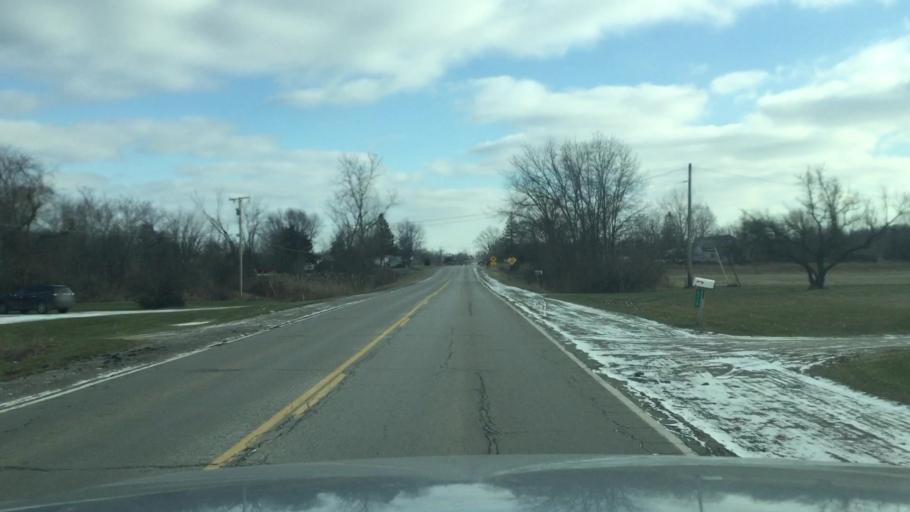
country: US
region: Michigan
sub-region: Genesee County
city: Lake Fenton
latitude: 42.8630
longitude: -83.7542
